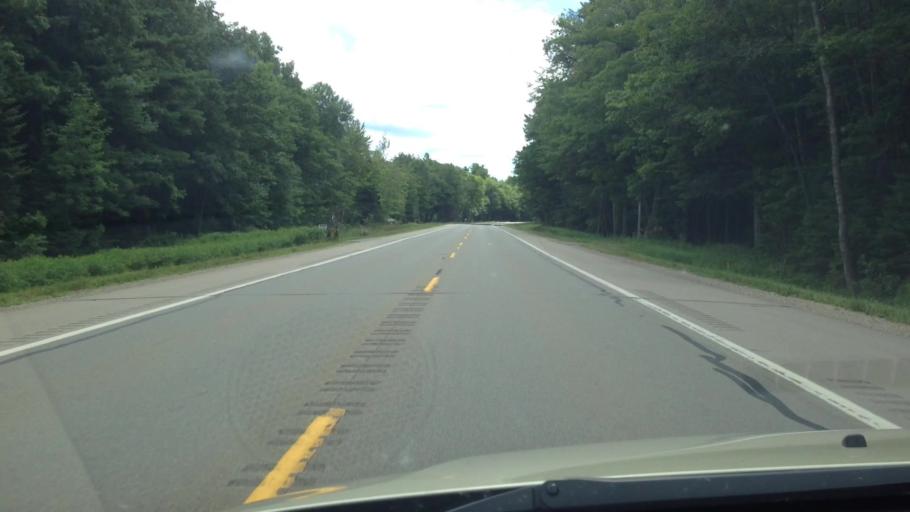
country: US
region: Michigan
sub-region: Menominee County
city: Menominee
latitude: 45.3026
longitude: -87.4396
